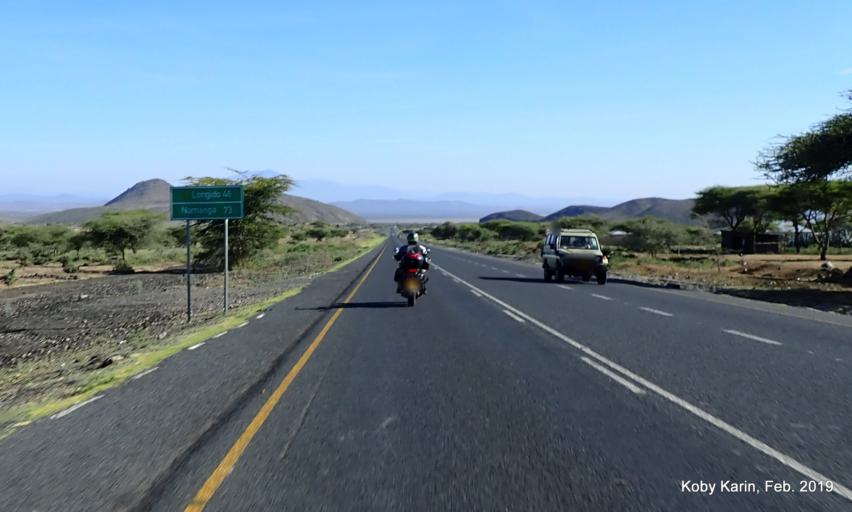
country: TZ
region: Arusha
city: Nkoaranga
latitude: -3.1386
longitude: 36.6934
